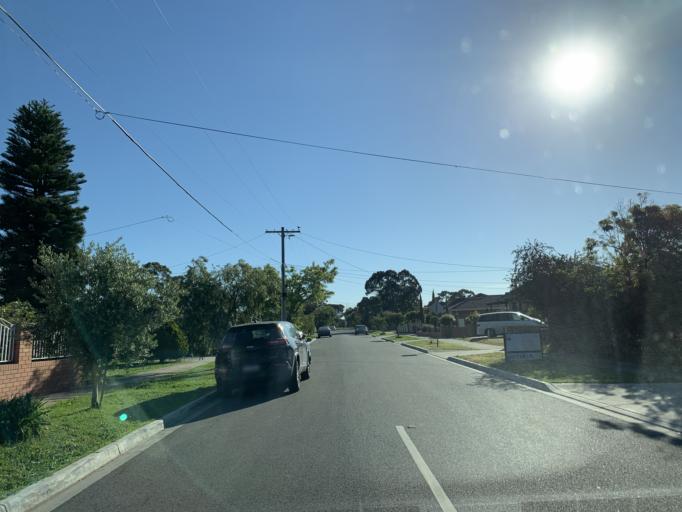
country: AU
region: Victoria
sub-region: Brimbank
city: St Albans
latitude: -37.7551
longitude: 144.8048
